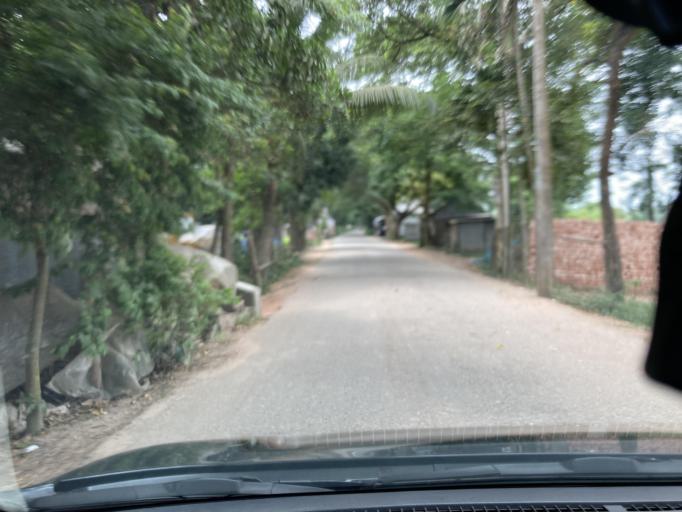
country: BD
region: Dhaka
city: Dohar
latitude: 23.8053
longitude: 90.0463
